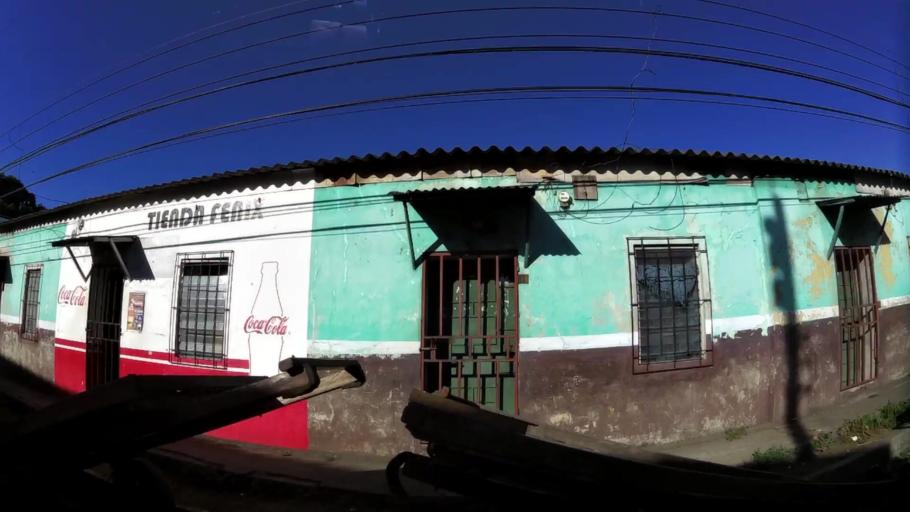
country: SV
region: Sonsonate
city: San Antonio del Monte
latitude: 13.7158
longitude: -89.7325
